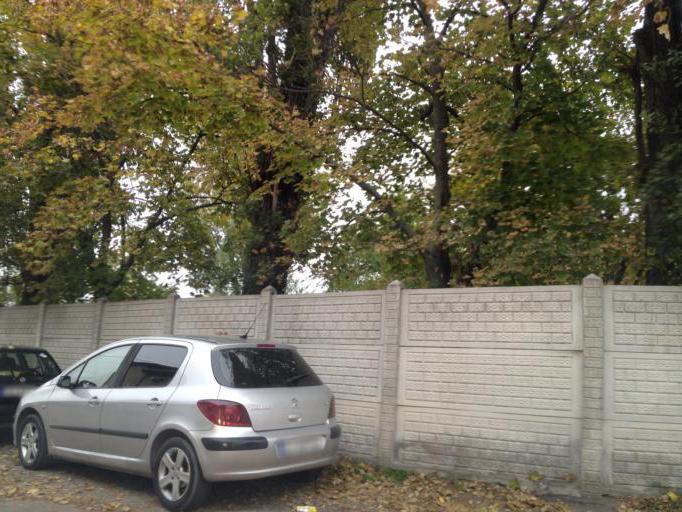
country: RO
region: Dolj
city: Craiova
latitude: 44.3039
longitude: 23.7892
